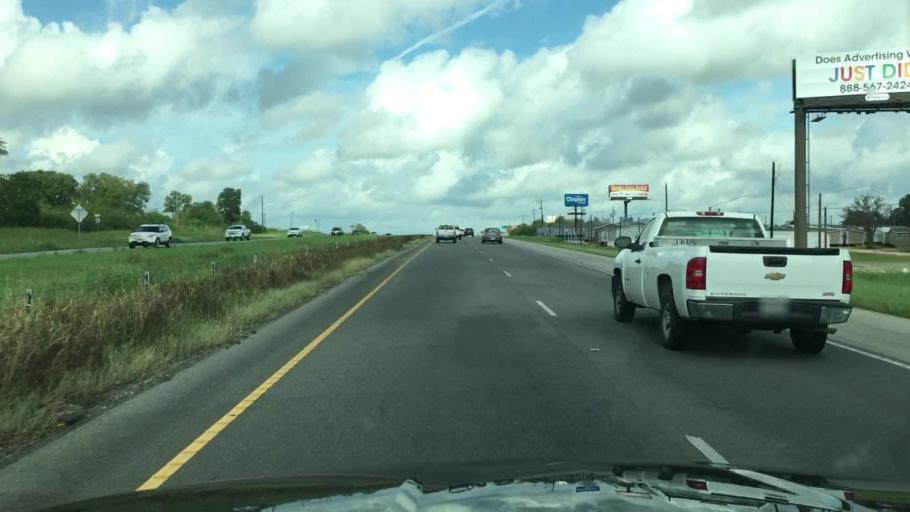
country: US
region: Texas
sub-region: Bastrop County
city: Wyldwood
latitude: 30.1573
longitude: -97.4975
